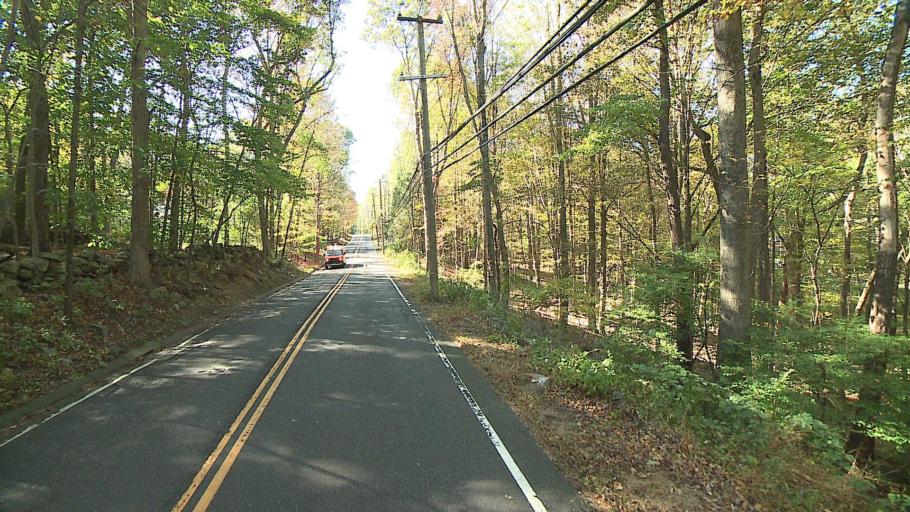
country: US
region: Connecticut
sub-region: Fairfield County
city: Westport
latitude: 41.1960
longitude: -73.3351
